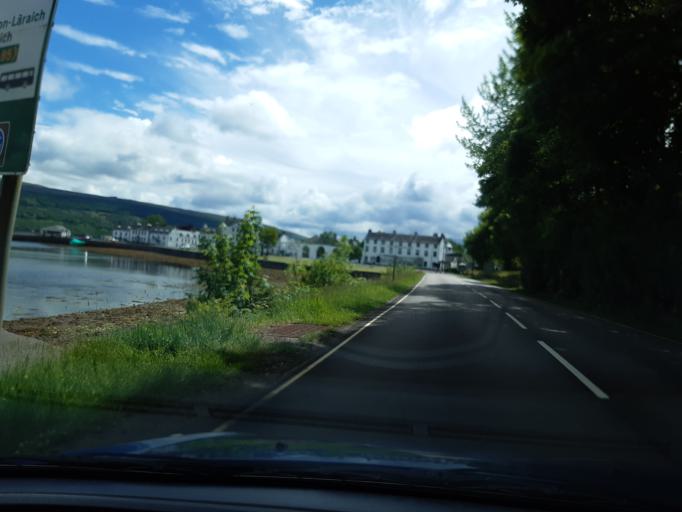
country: GB
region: Scotland
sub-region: Argyll and Bute
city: Garelochhead
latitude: 56.2336
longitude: -5.0734
